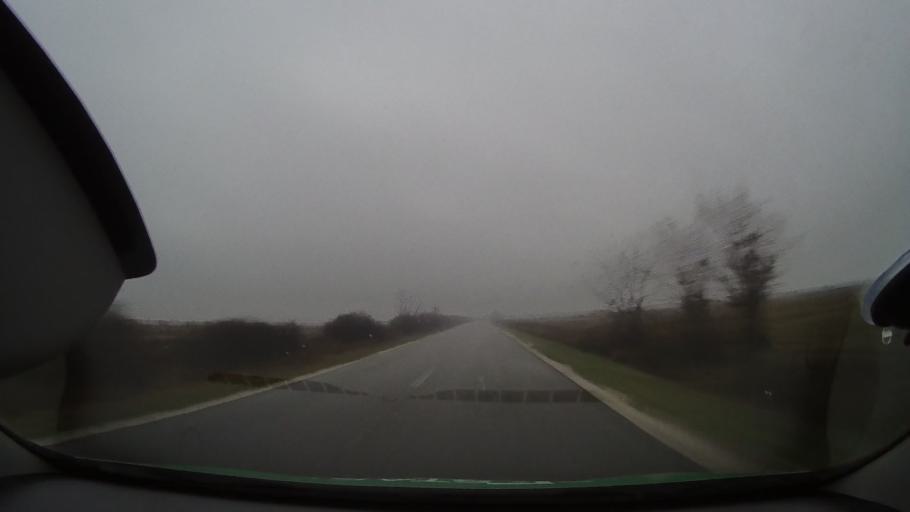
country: RO
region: Arad
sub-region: Comuna Craiova
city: Craiova
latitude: 46.6082
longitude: 21.9580
